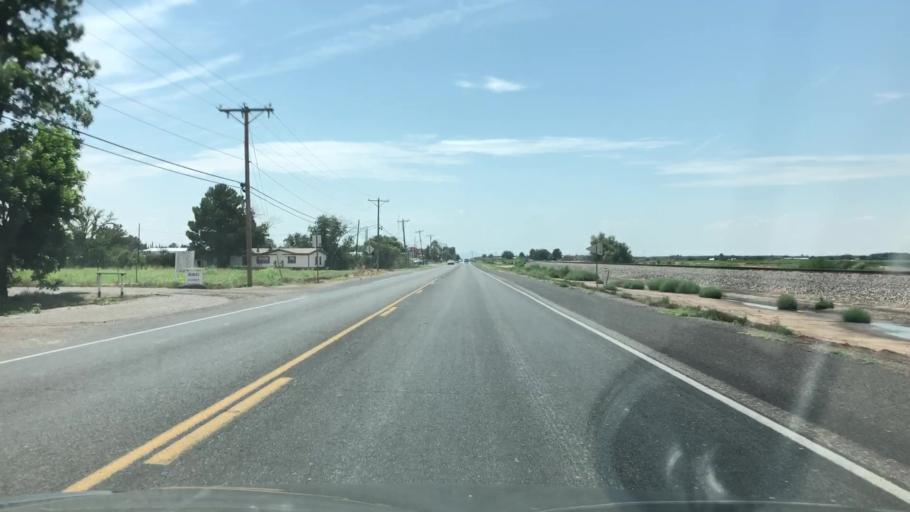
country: US
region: New Mexico
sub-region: Dona Ana County
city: University Park
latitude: 32.2474
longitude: -106.7489
